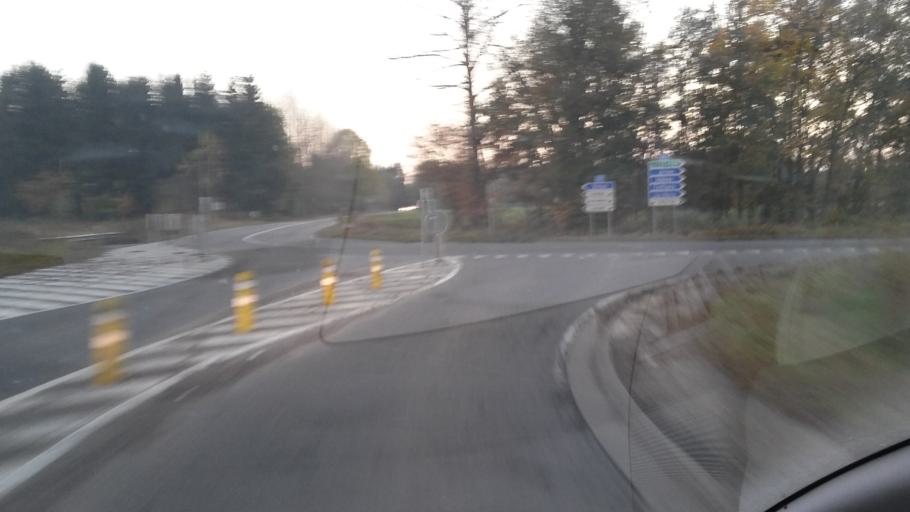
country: BE
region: Wallonia
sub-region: Province du Luxembourg
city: Etalle
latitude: 49.6643
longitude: 5.5969
